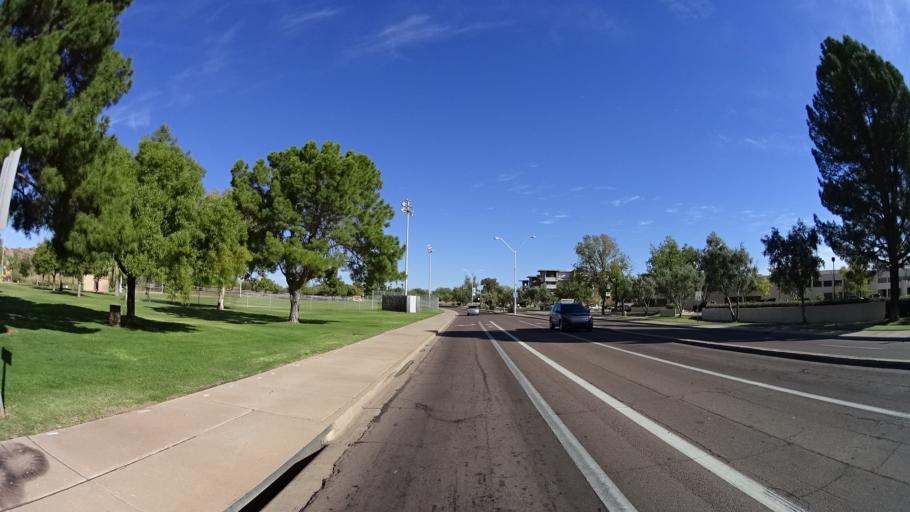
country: US
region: Arizona
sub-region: Maricopa County
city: Tempe Junction
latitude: 33.4405
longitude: -111.9309
